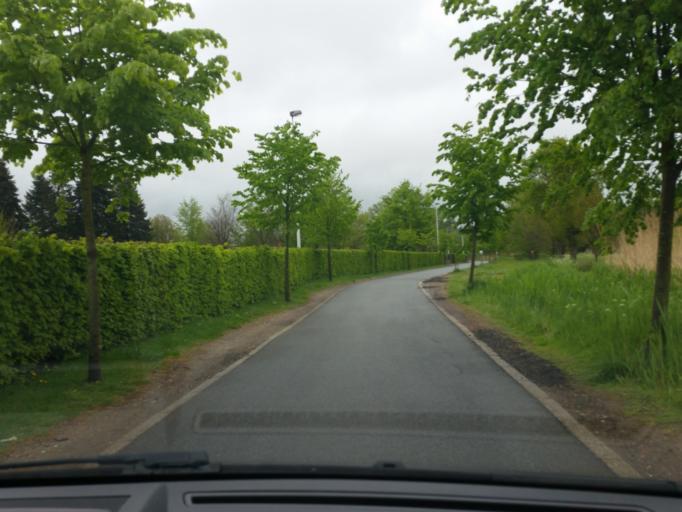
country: BE
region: Flanders
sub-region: Provincie Antwerpen
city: Borsbeek
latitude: 51.1921
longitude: 4.4808
